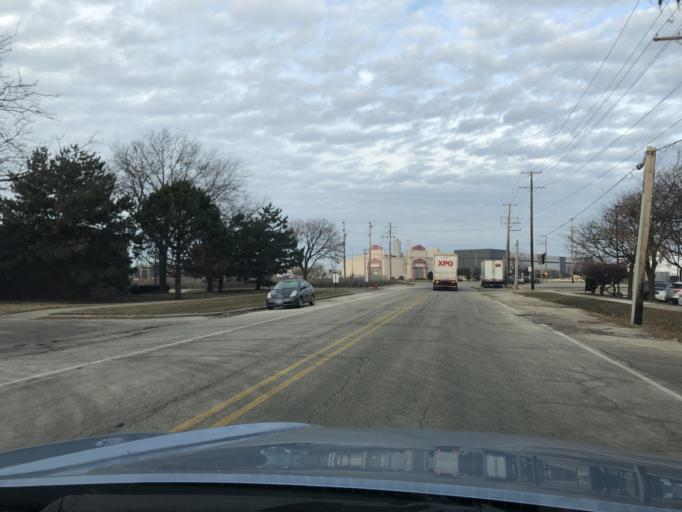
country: US
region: Illinois
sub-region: Cook County
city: Elk Grove Village
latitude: 42.0067
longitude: -87.9383
